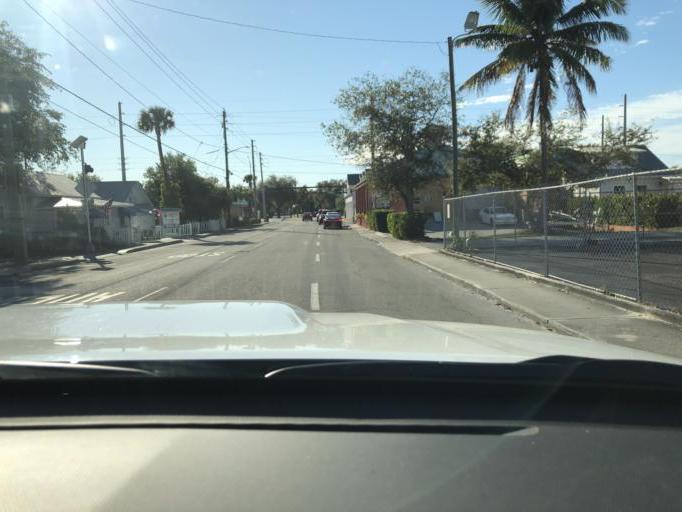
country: US
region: Florida
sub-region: Martin County
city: Stuart
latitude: 27.1976
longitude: -80.2556
